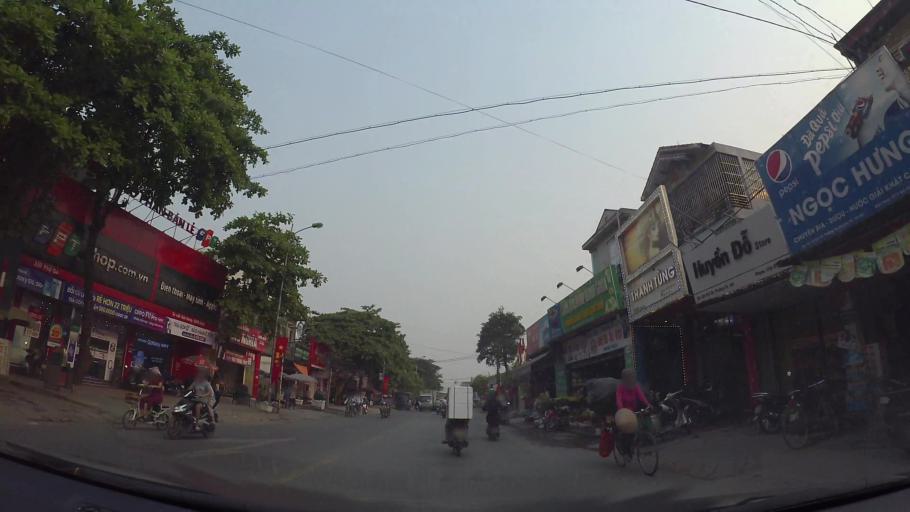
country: VN
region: Ha Noi
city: Thuong Tin
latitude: 20.8711
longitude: 105.8647
